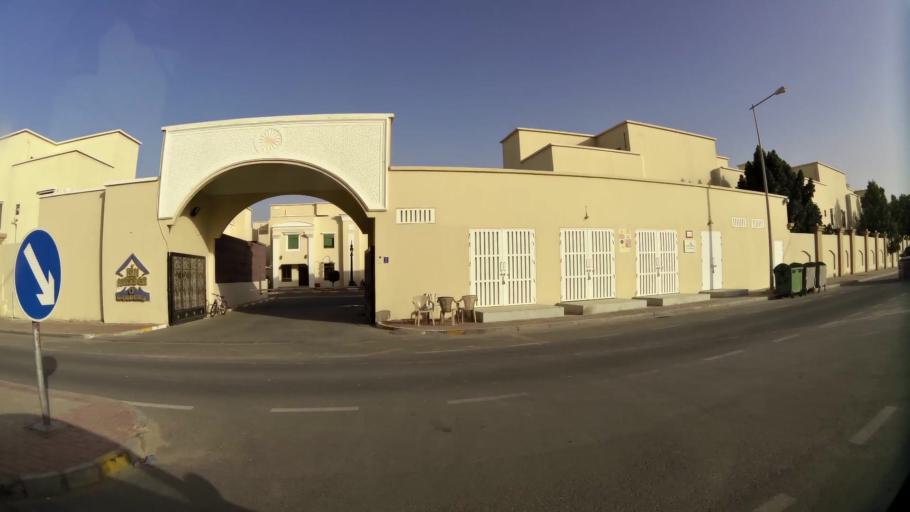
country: QA
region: Baladiyat ar Rayyan
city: Ar Rayyan
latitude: 25.3348
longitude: 51.4563
